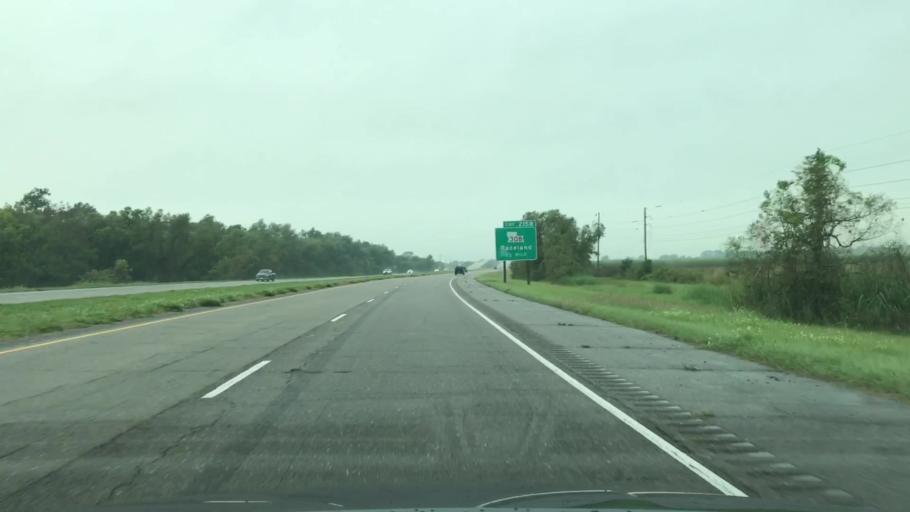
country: US
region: Louisiana
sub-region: Lafourche Parish
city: Mathews
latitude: 29.7190
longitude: -90.5621
